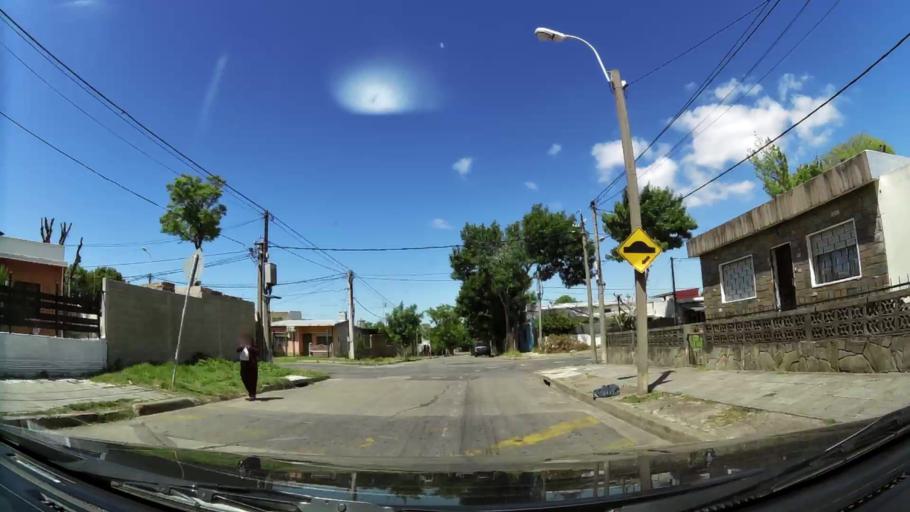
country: UY
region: Montevideo
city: Montevideo
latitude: -34.8570
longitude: -56.1375
